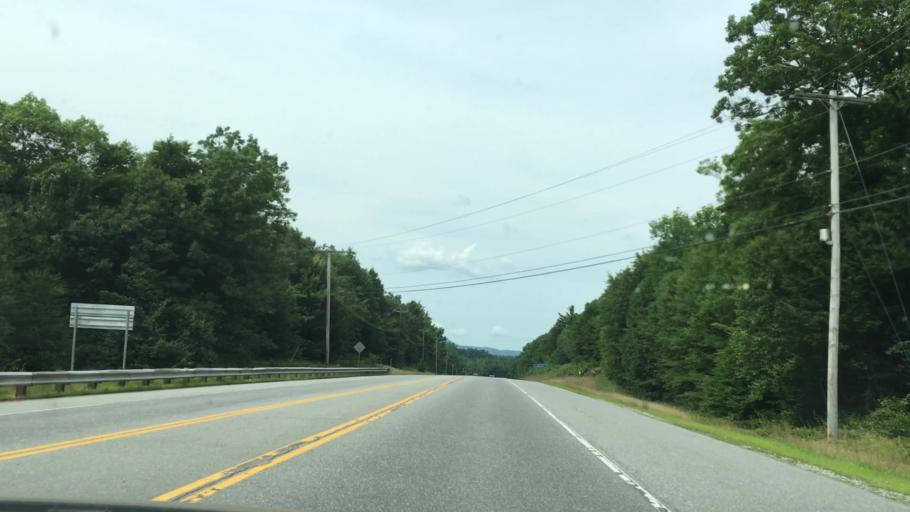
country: US
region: New Hampshire
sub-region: Cheshire County
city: Rindge
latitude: 42.7446
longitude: -72.0382
